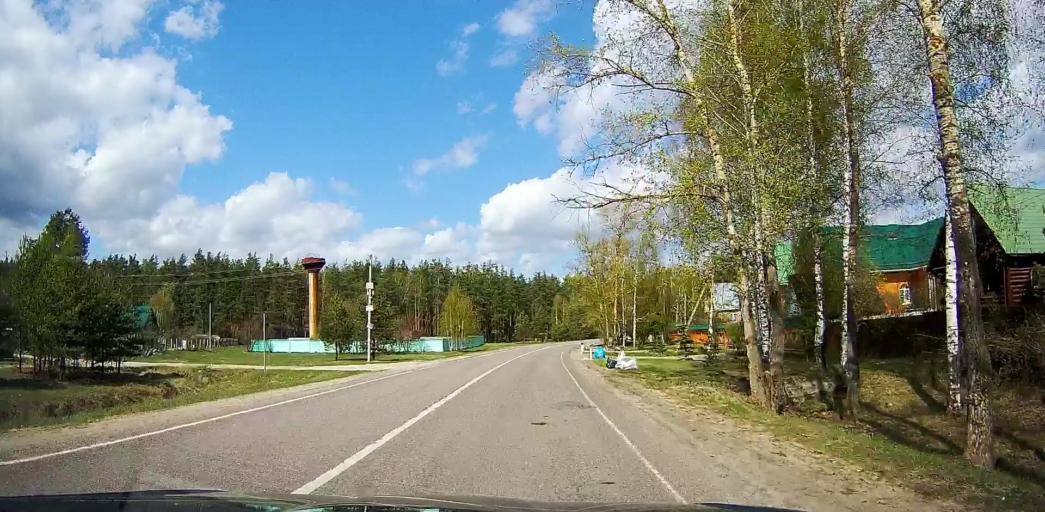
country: RU
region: Moskovskaya
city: Davydovo
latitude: 55.5618
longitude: 38.8131
